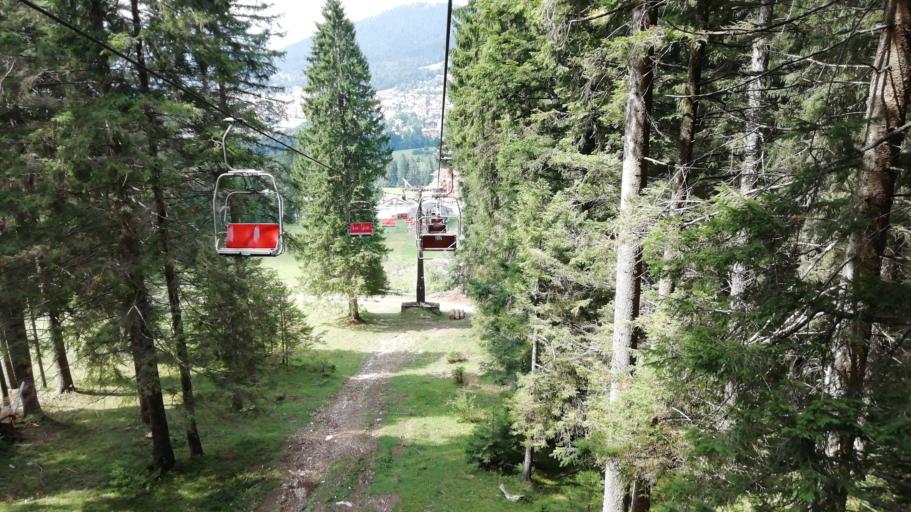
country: IT
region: Trentino-Alto Adige
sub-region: Provincia di Trento
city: Folgaria
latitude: 45.9035
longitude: 11.1881
